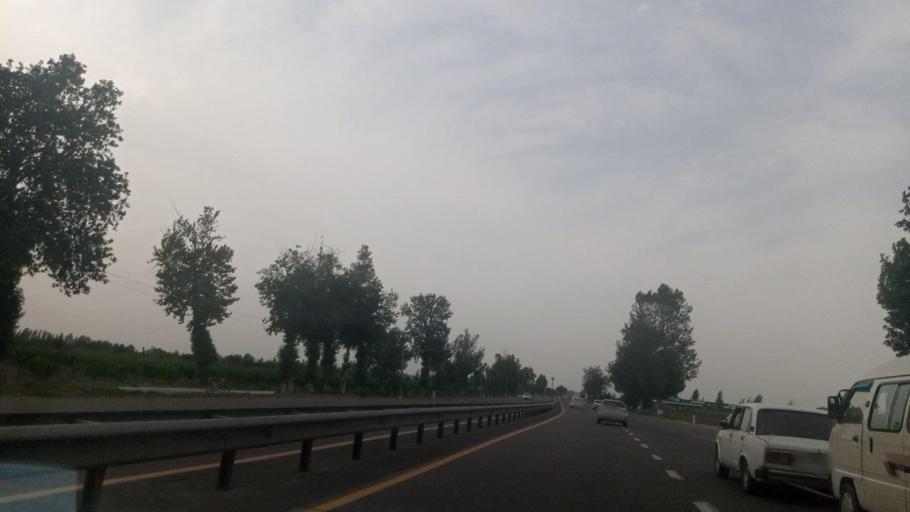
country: UZ
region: Toshkent Shahri
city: Bektemir
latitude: 41.1444
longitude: 69.4318
